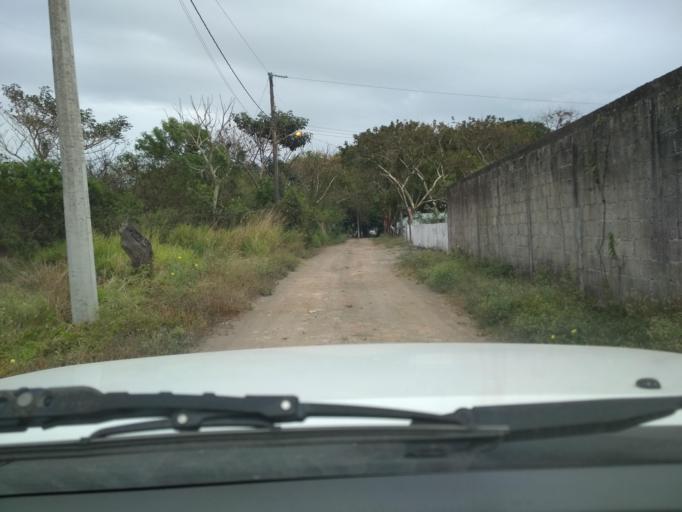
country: MX
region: Veracruz
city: El Tejar
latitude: 19.0675
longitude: -96.1356
